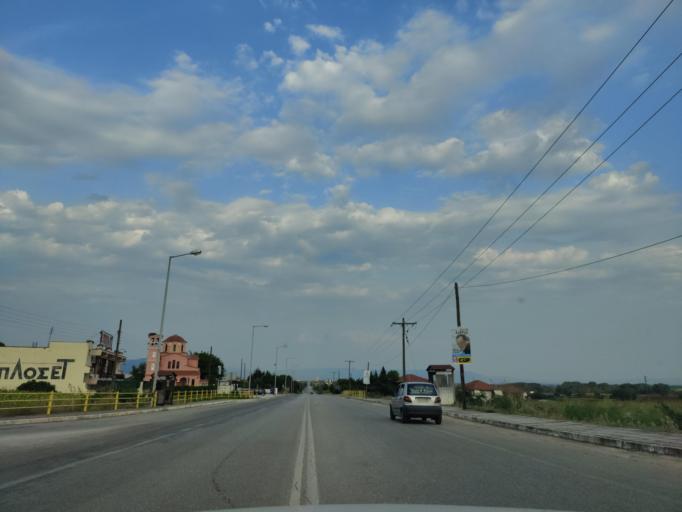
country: GR
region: East Macedonia and Thrace
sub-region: Nomos Dramas
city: Petroussa
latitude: 41.1688
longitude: 24.0446
